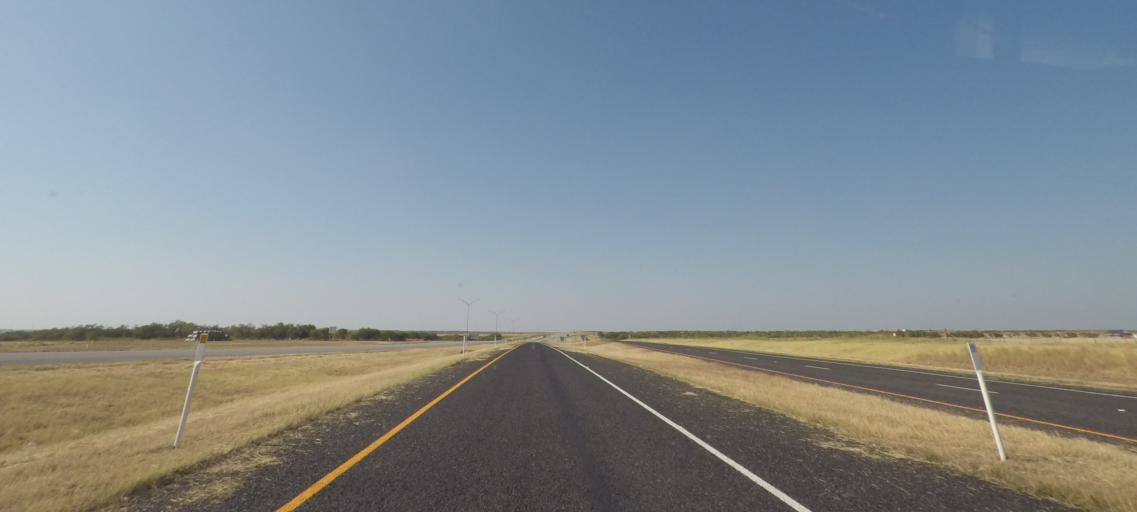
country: US
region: Texas
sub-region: Baylor County
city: Seymour
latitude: 33.5994
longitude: -99.2412
